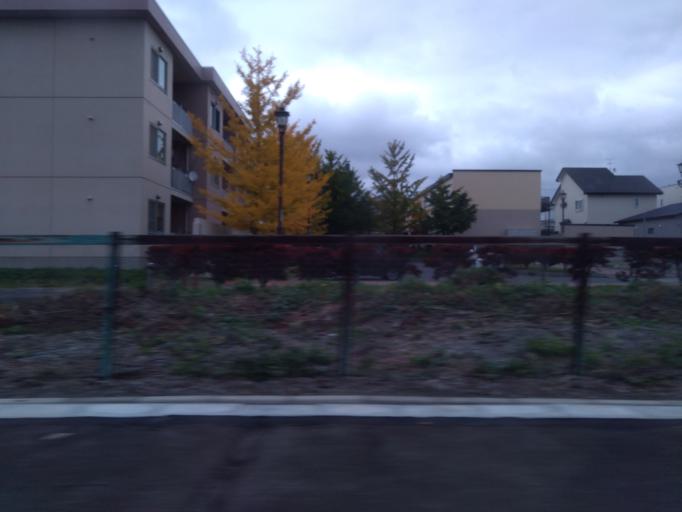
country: JP
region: Hokkaido
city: Nanae
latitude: 41.8882
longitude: 140.6876
